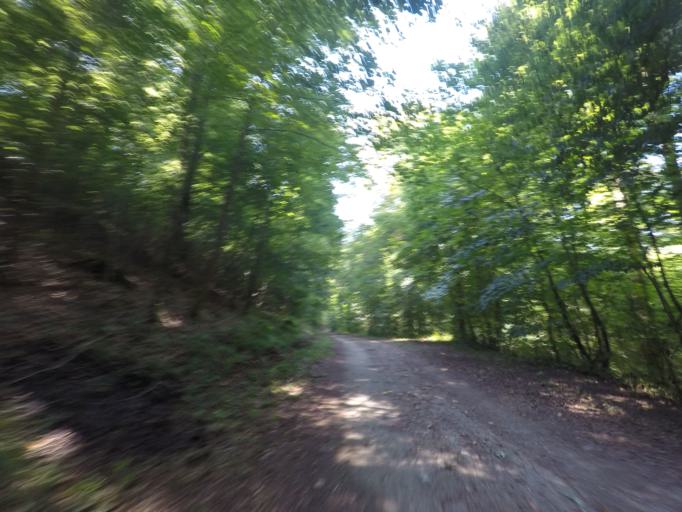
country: LU
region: Luxembourg
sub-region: Canton de Capellen
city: Kopstal
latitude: 49.6527
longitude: 6.0639
